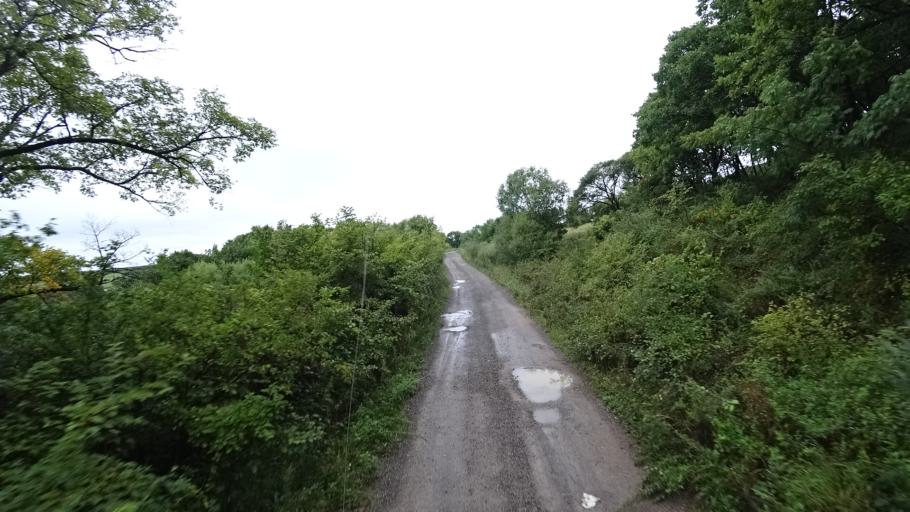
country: RU
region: Primorskiy
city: Monastyrishche
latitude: 44.2610
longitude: 132.4067
